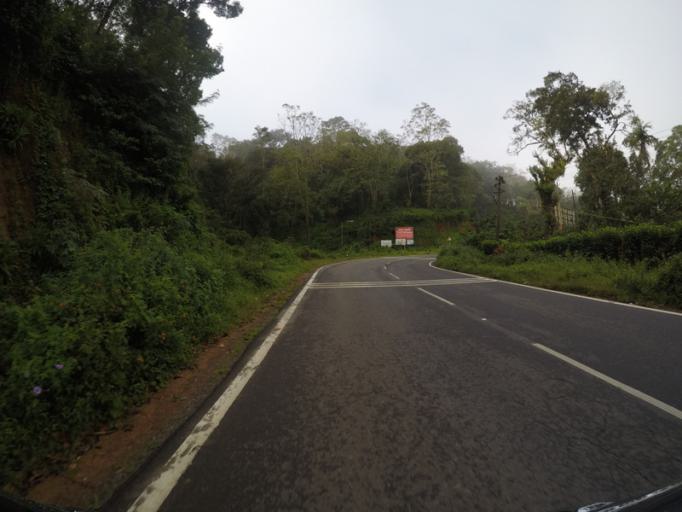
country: IN
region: Karnataka
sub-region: Kodagu
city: Madikeri
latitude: 12.4302
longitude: 75.7837
